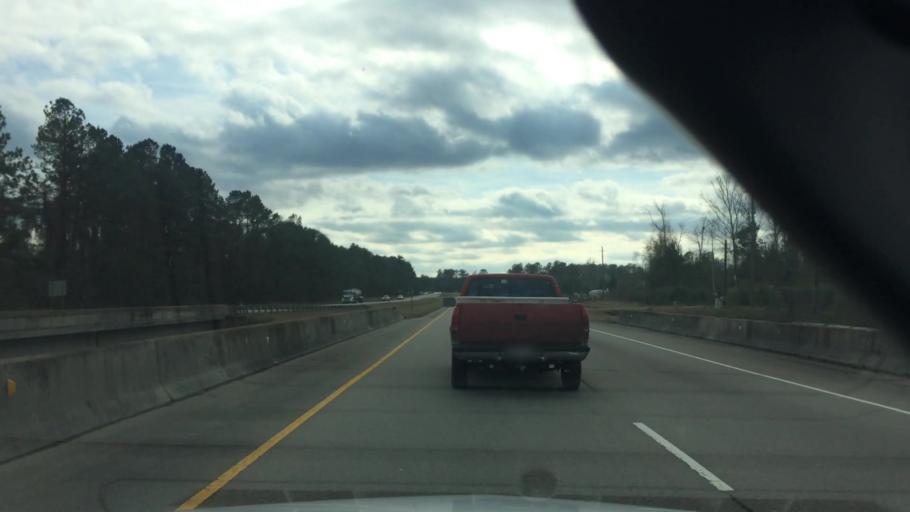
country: US
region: North Carolina
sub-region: Brunswick County
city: Bolivia
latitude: 34.1569
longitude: -78.0921
